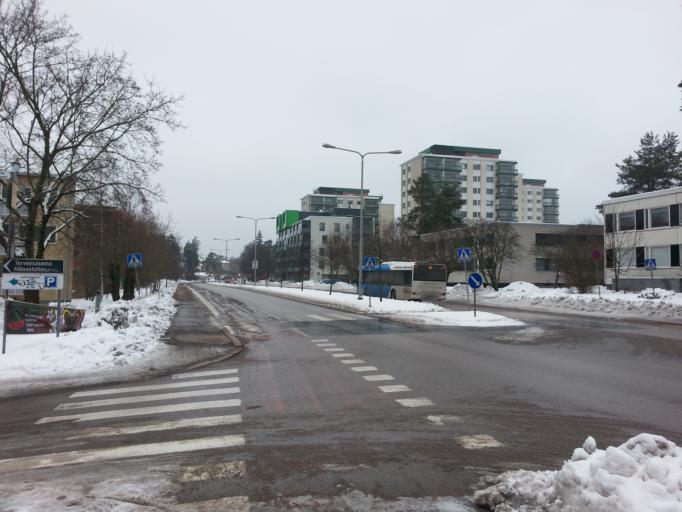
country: FI
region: Uusimaa
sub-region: Helsinki
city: Teekkarikylae
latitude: 60.2269
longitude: 24.8531
